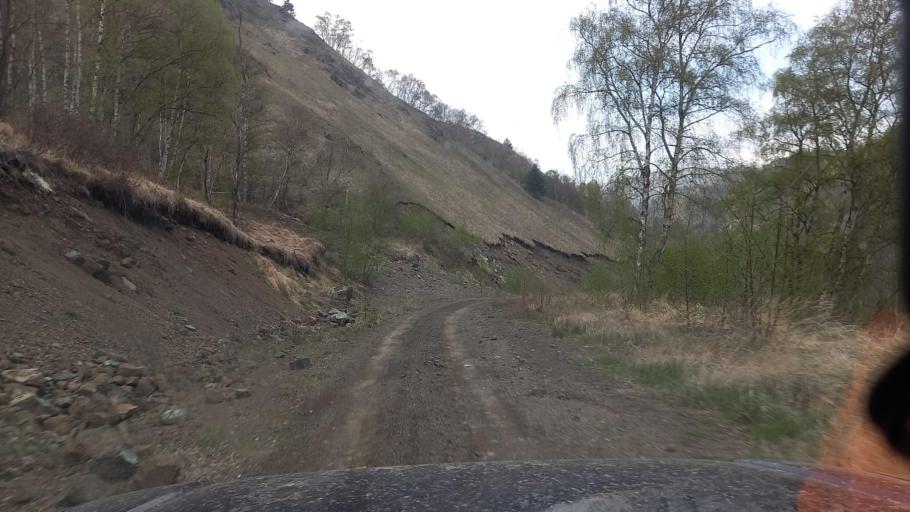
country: RU
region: Kabardino-Balkariya
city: Kamennomostskoye
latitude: 43.7024
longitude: 42.8437
